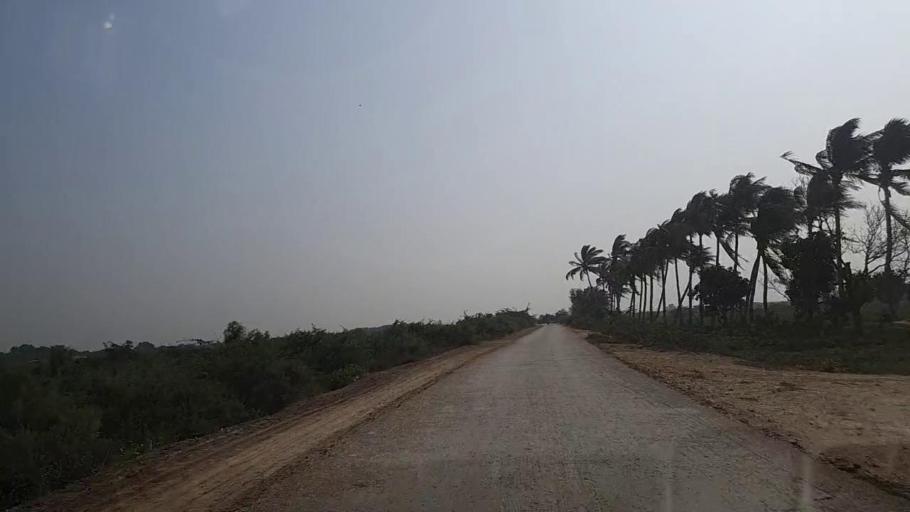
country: PK
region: Sindh
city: Keti Bandar
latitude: 24.2433
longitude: 67.6367
